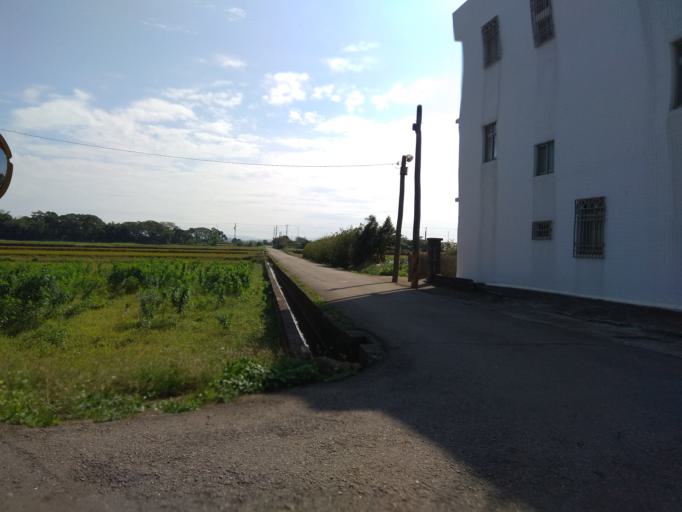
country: TW
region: Taiwan
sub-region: Hsinchu
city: Zhubei
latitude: 24.9480
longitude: 121.0049
